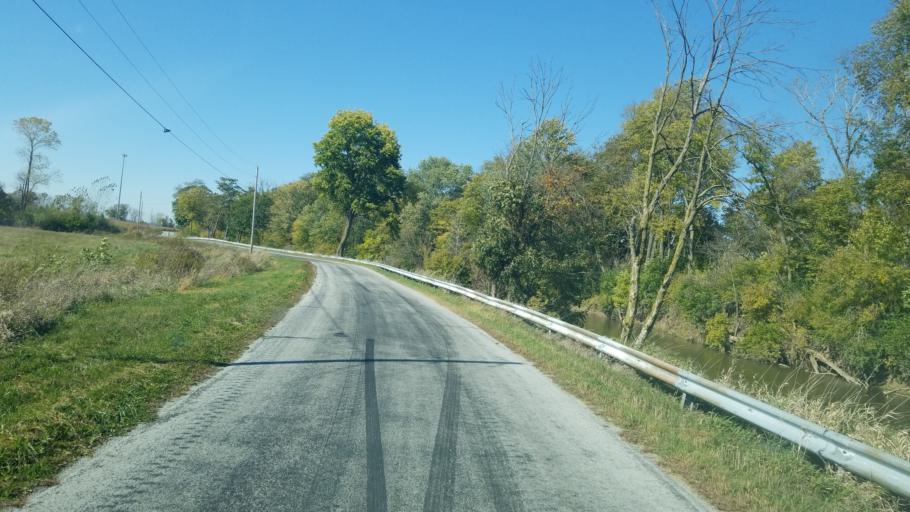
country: US
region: Ohio
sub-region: Hardin County
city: Kenton
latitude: 40.6336
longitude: -83.5625
